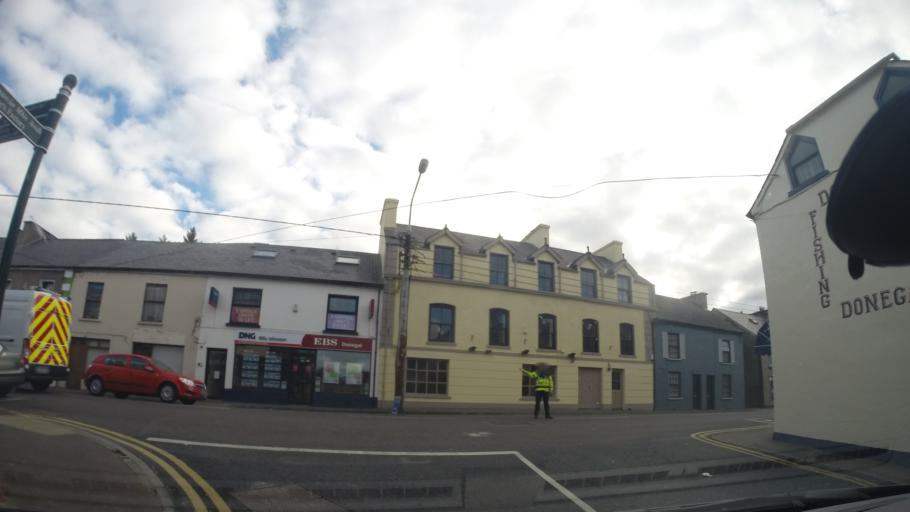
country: IE
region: Ulster
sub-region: County Donegal
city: Donegal
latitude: 54.6544
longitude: -8.1076
